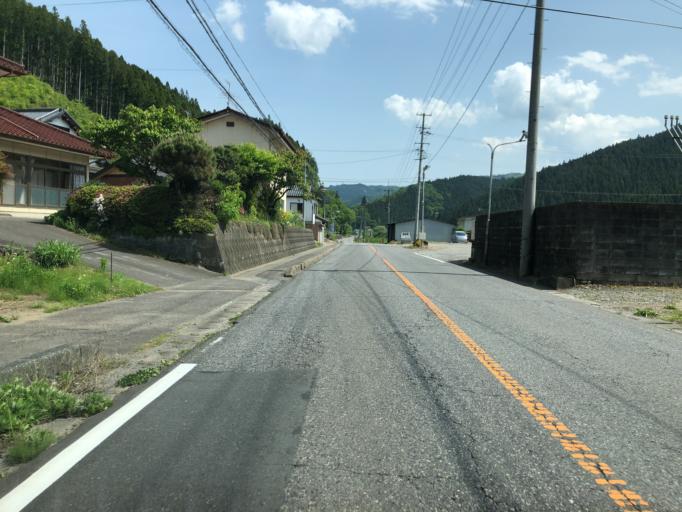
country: JP
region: Fukushima
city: Ishikawa
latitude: 37.0732
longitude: 140.5759
